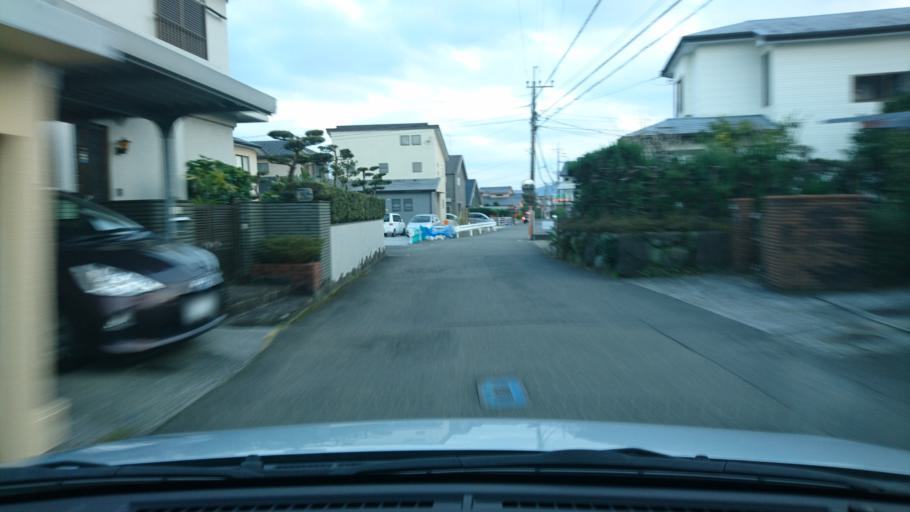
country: JP
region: Miyazaki
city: Miyazaki-shi
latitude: 31.8578
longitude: 131.4304
